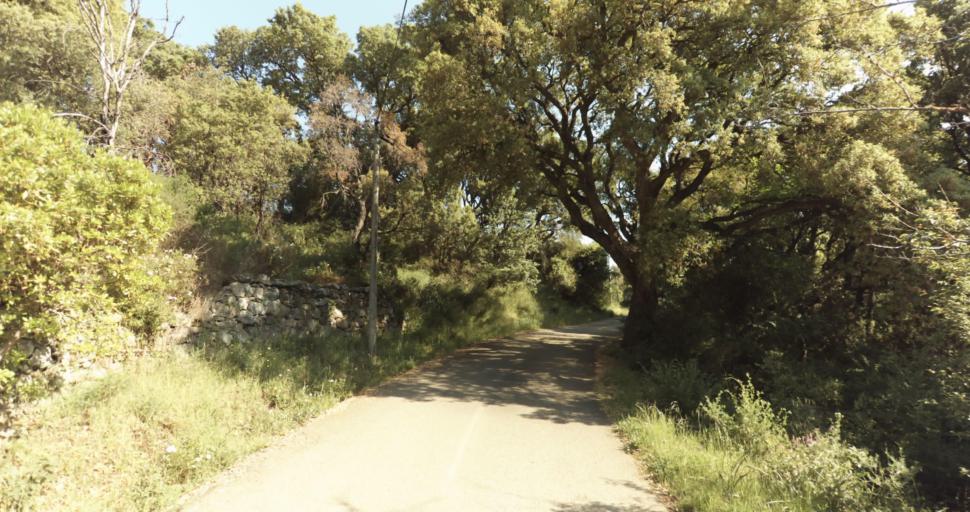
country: FR
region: Corsica
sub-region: Departement de la Haute-Corse
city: Furiani
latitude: 42.6385
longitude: 9.4161
